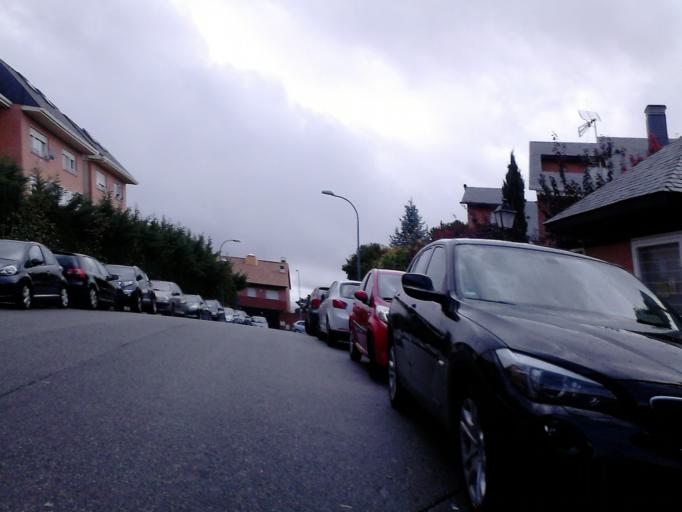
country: ES
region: Madrid
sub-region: Provincia de Madrid
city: Torrelodones
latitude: 40.5697
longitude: -3.9254
